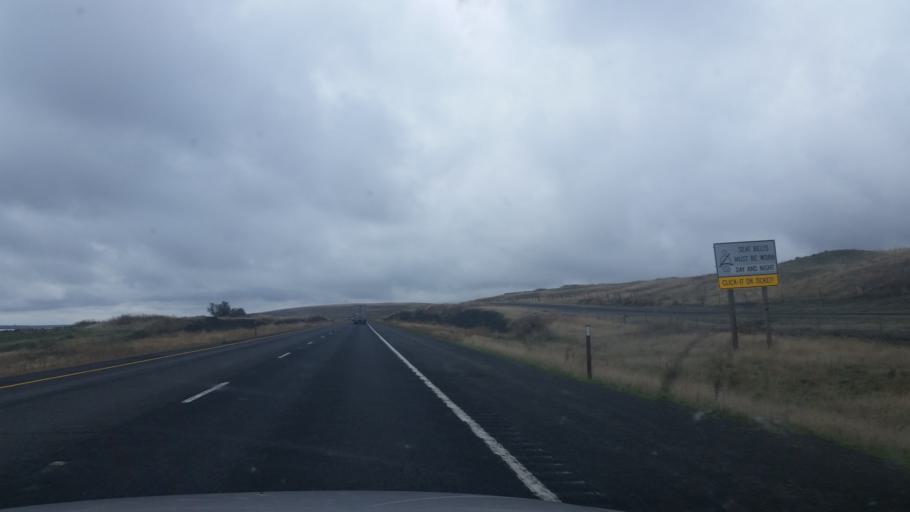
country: US
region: Washington
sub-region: Adams County
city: Ritzville
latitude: 47.2833
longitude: -118.0456
